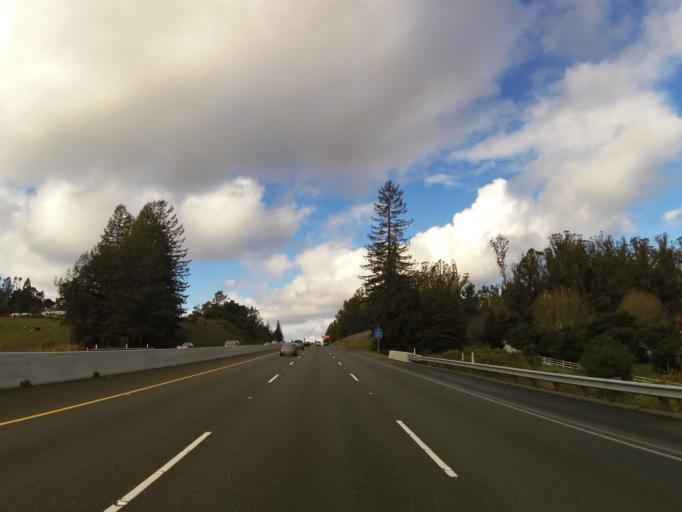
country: US
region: California
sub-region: Sonoma County
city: Cotati
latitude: 38.3050
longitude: -122.7093
